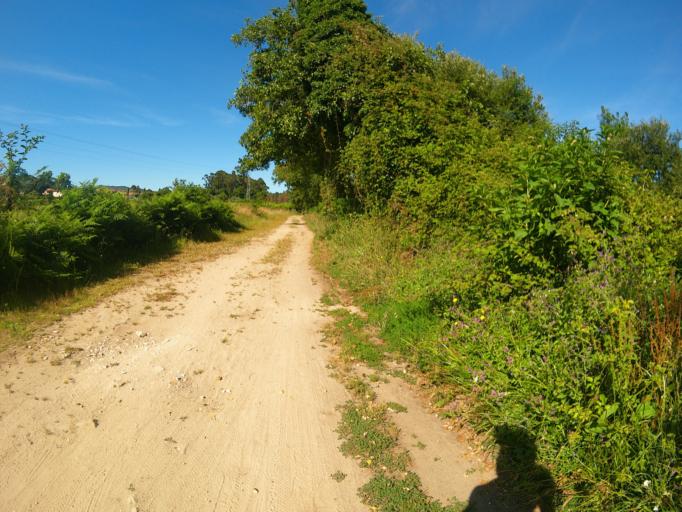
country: PT
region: Viana do Castelo
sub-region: Ponte de Lima
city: Ponte de Lima
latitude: 41.7374
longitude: -8.6497
